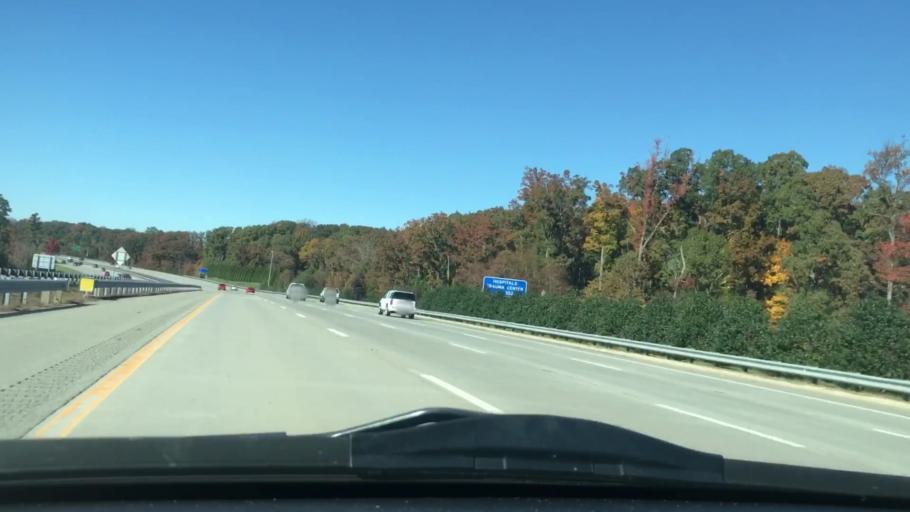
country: US
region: North Carolina
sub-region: Guilford County
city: Jamestown
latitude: 36.0377
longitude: -79.8907
